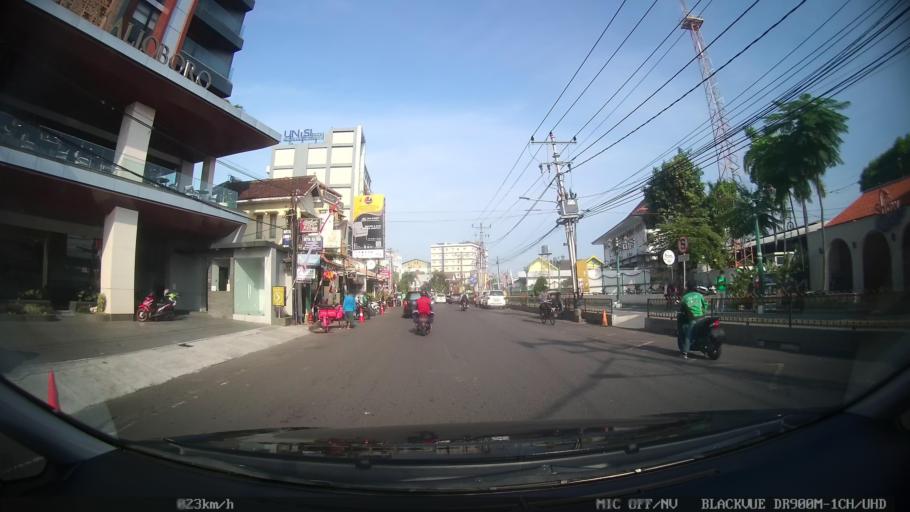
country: ID
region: Daerah Istimewa Yogyakarta
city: Yogyakarta
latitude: -7.7899
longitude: 110.3645
